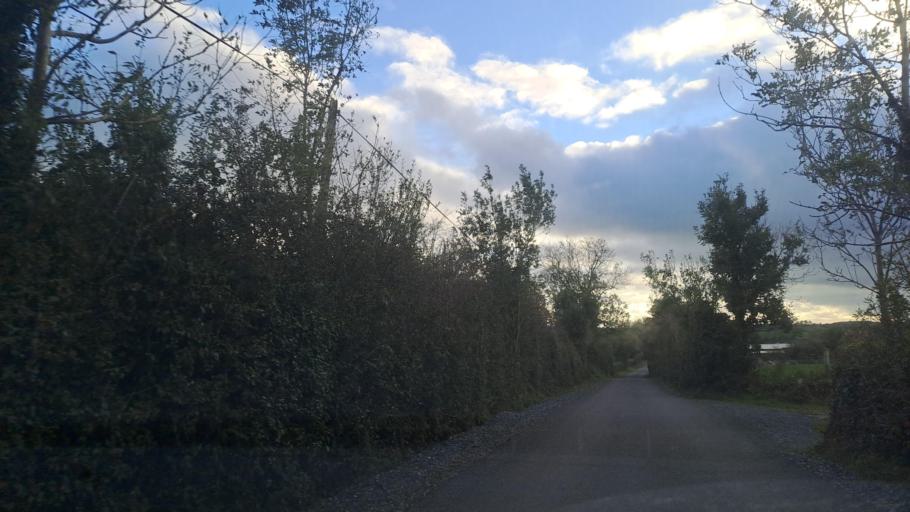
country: IE
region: Ulster
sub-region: County Monaghan
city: Castleblayney
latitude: 54.0400
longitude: -6.8069
